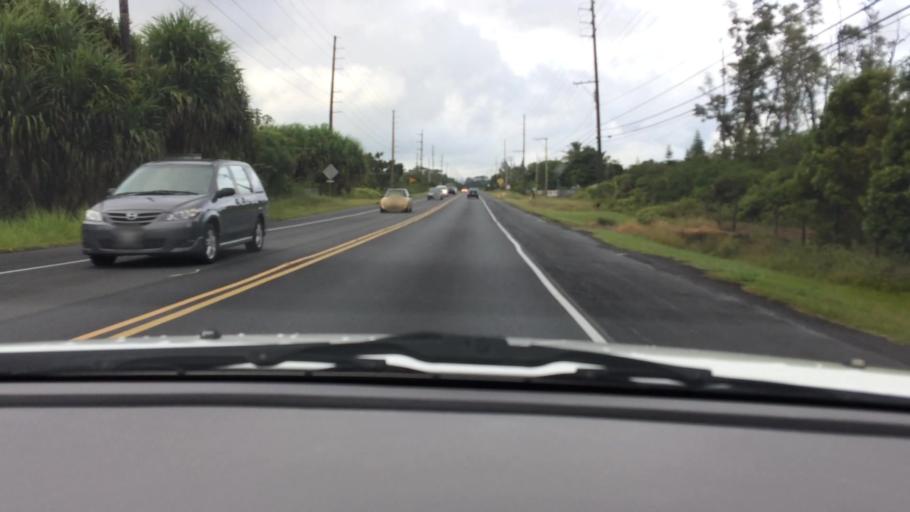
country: US
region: Hawaii
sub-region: Hawaii County
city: Orchidlands Estates
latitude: 19.5687
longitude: -154.9985
